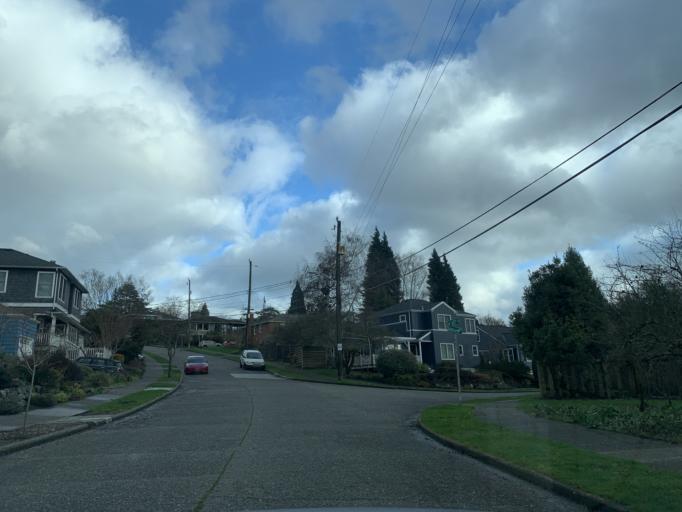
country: US
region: Washington
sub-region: King County
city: Yarrow Point
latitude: 47.6721
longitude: -122.2794
